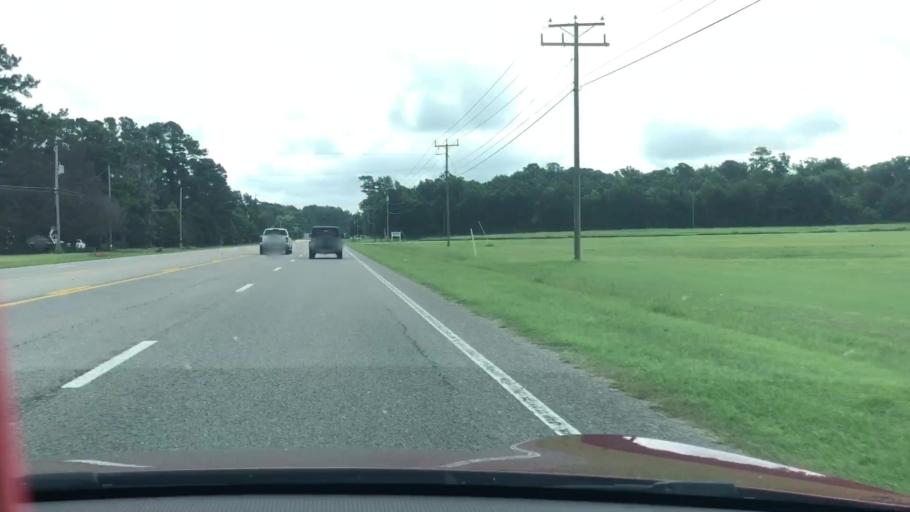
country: US
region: North Carolina
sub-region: Dare County
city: Southern Shores
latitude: 36.2601
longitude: -75.8986
